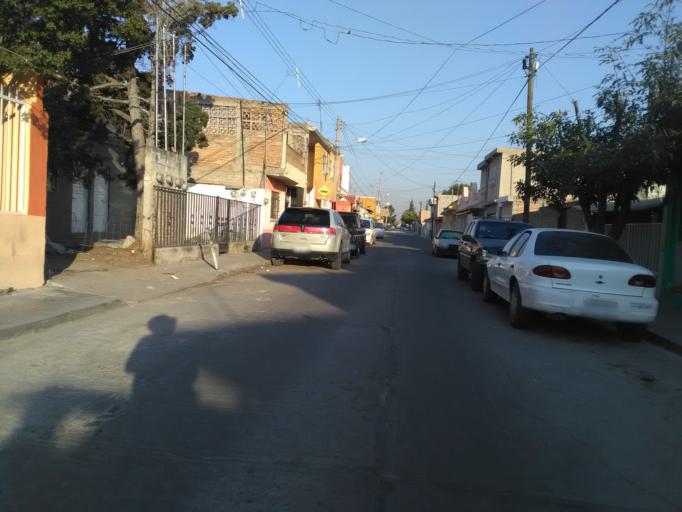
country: MX
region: Durango
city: Victoria de Durango
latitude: 24.0385
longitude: -104.6411
